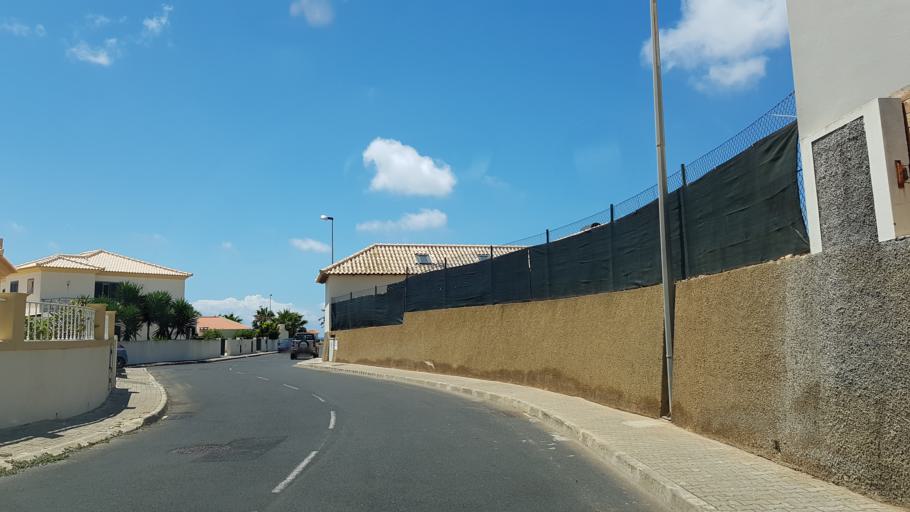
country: PT
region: Madeira
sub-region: Porto Santo
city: Vila de Porto Santo
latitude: 33.0564
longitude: -16.3564
